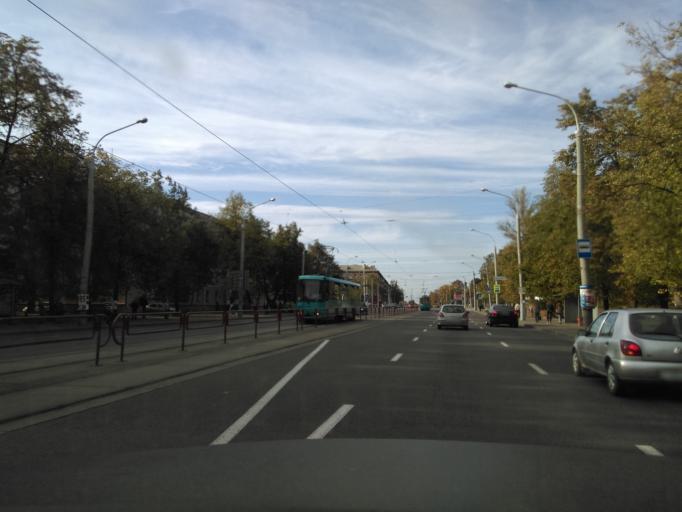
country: BY
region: Minsk
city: Minsk
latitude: 53.8858
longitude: 27.6193
